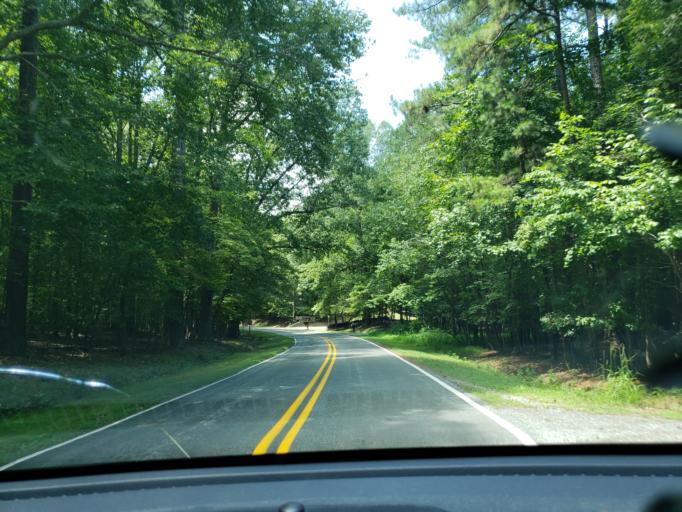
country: US
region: North Carolina
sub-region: Orange County
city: Hillsborough
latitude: 36.0786
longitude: -79.0026
